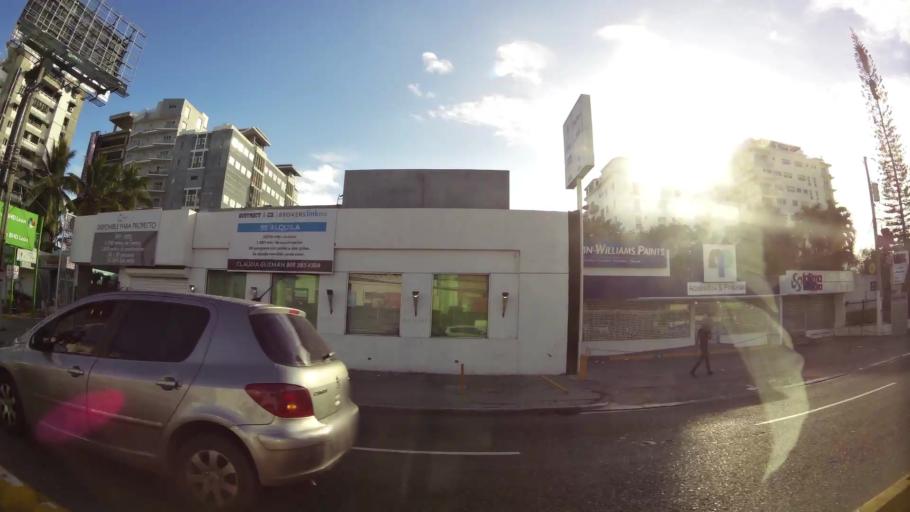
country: DO
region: Nacional
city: La Julia
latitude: 18.4741
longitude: -69.9262
